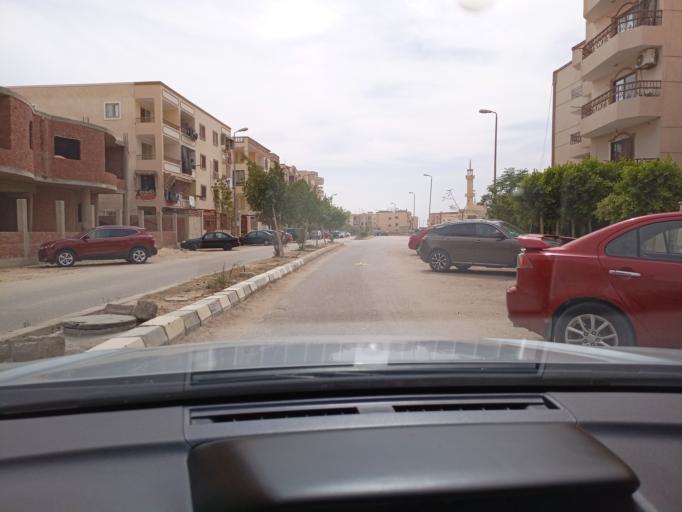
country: EG
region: Muhafazat al Qalyubiyah
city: Al Khankah
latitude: 30.2415
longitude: 31.4857
